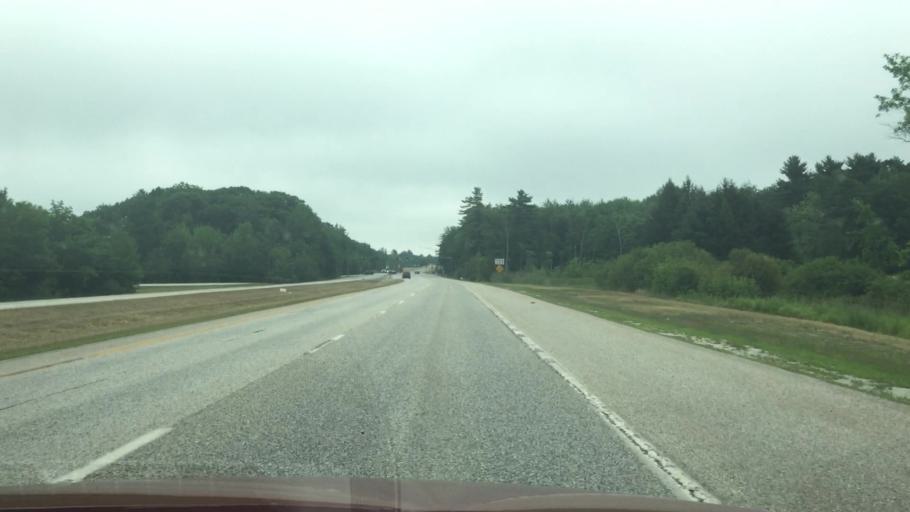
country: US
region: Maine
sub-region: Cumberland County
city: Westbrook
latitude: 43.6720
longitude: -70.3406
